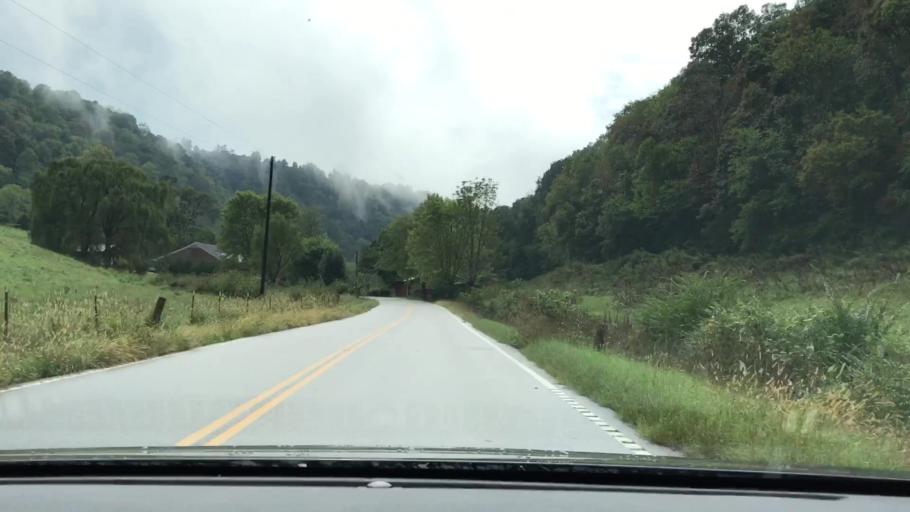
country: US
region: Tennessee
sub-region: Macon County
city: Red Boiling Springs
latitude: 36.4132
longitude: -85.9299
